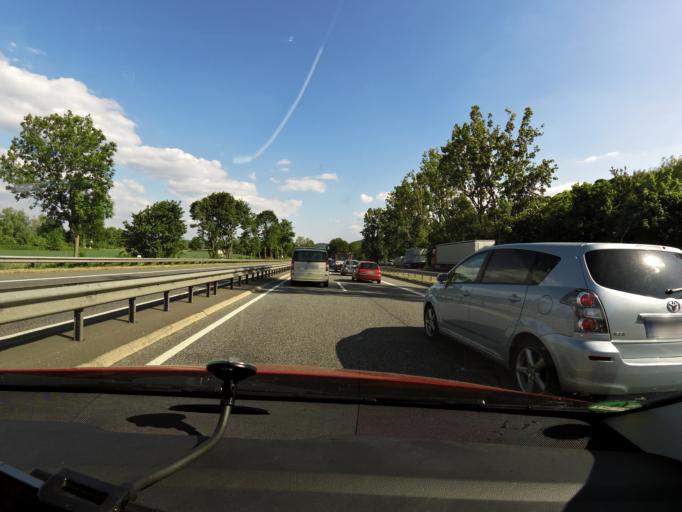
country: DE
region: Rheinland-Pfalz
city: Bad Breisig
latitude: 50.5220
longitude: 7.2867
